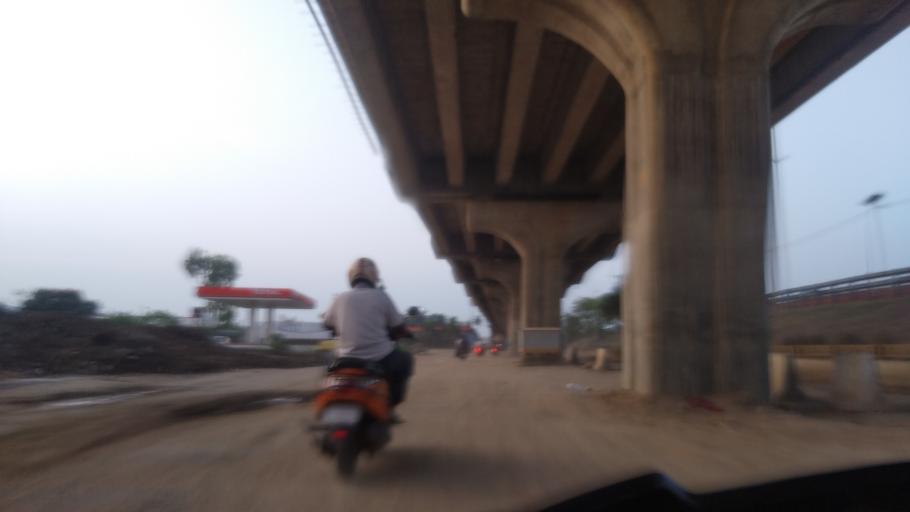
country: IN
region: Tamil Nadu
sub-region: Coimbatore
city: Coimbatore
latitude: 10.9836
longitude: 76.9617
